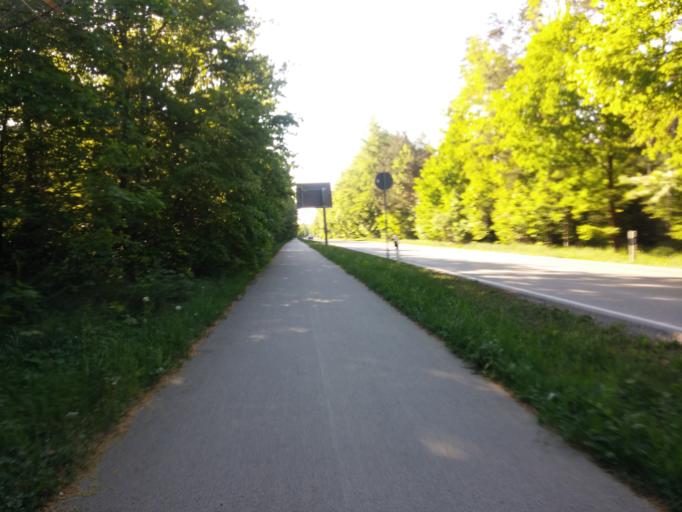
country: DE
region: Bavaria
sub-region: Upper Bavaria
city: Vaterstetten
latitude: 48.1168
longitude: 11.7664
